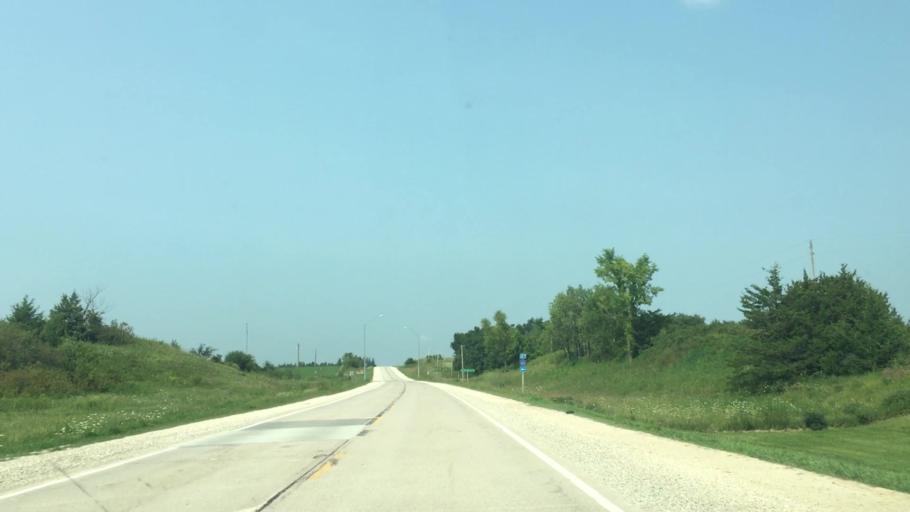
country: US
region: Iowa
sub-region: Fayette County
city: West Union
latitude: 43.1271
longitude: -91.8692
